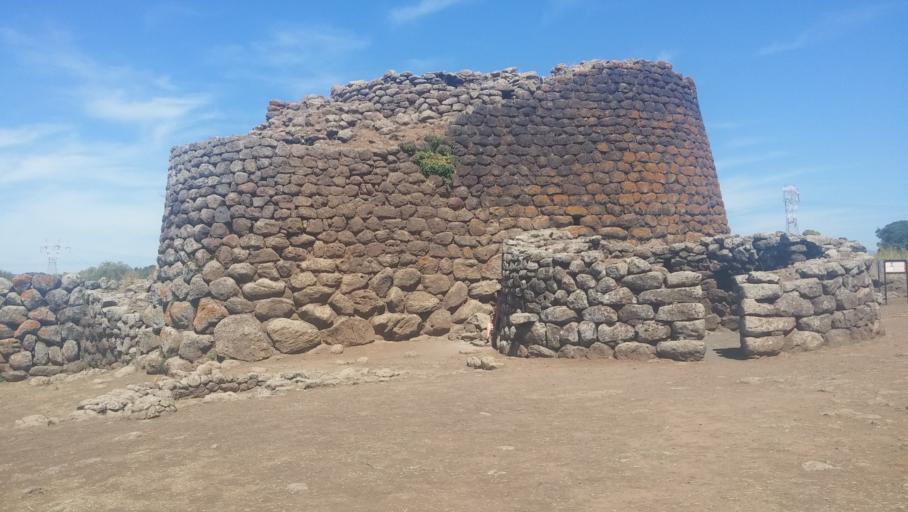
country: IT
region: Sardinia
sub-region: Provincia di Oristano
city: Abbasanta
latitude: 40.1165
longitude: 8.7903
